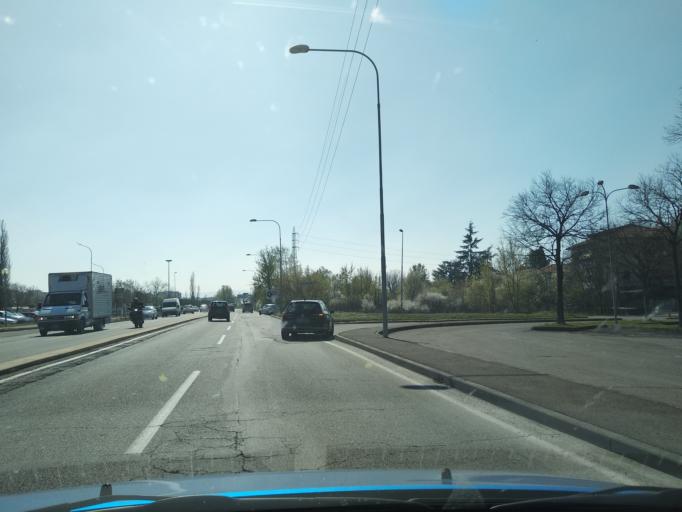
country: IT
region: Emilia-Romagna
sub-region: Provincia di Reggio Emilia
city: Reggio nell'Emilia
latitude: 44.6945
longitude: 10.6094
